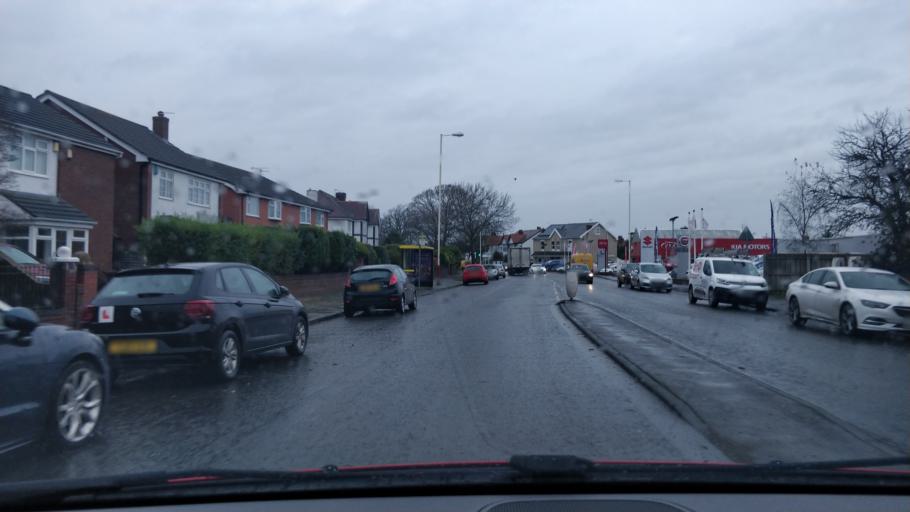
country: GB
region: England
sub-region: Sefton
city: Formby
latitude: 53.5994
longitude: -3.0344
